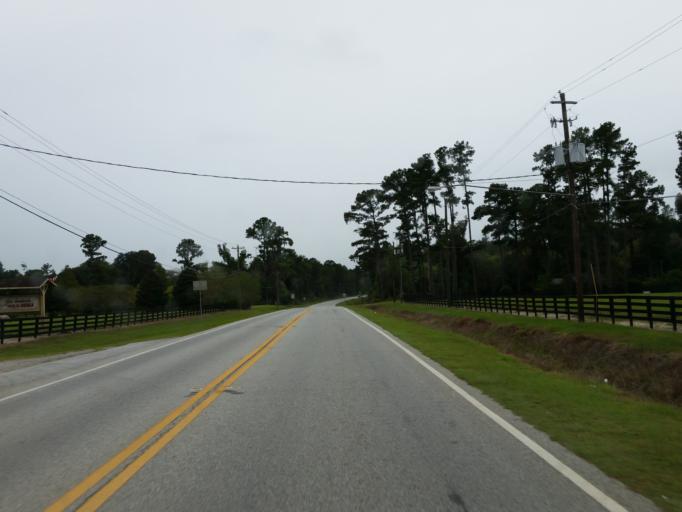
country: US
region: Georgia
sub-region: Lanier County
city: Lakeland
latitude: 31.0420
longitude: -83.0911
